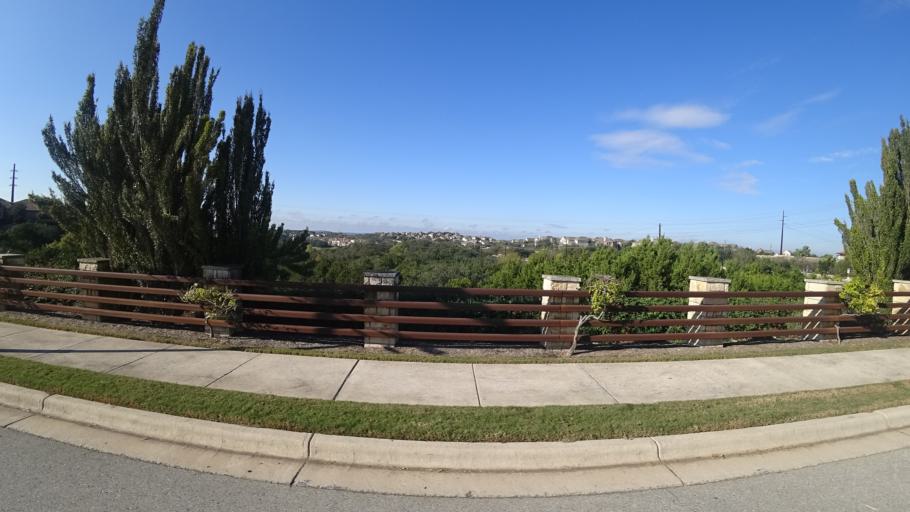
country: US
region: Texas
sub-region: Travis County
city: Hudson Bend
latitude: 30.3686
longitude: -97.8915
